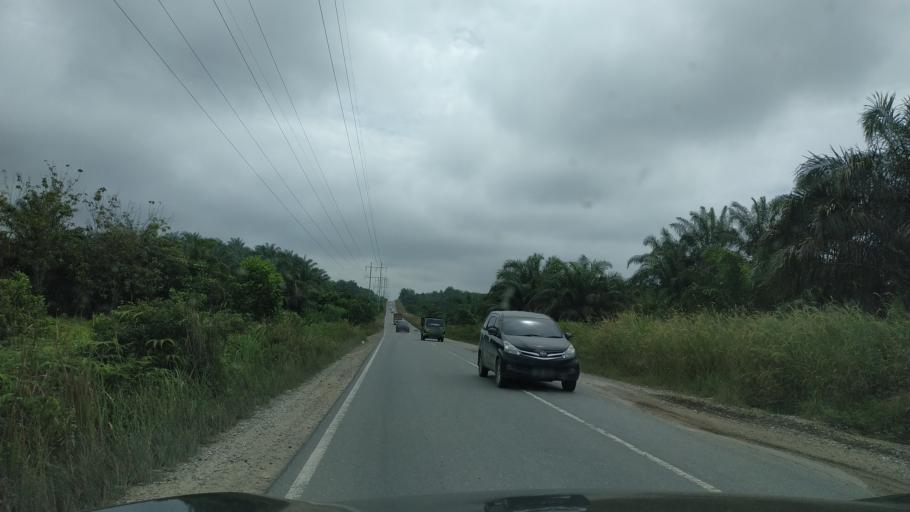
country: ID
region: Riau
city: Pekanbaru
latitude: 0.6435
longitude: 101.6703
